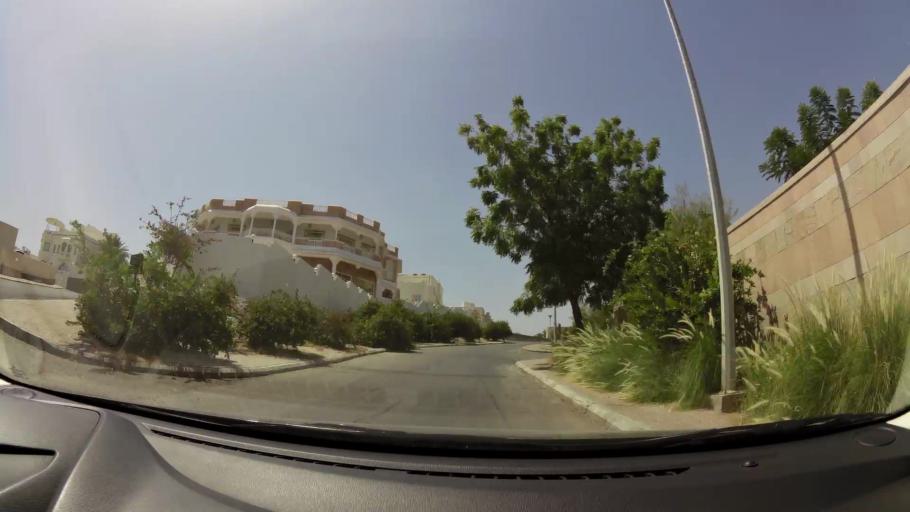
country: OM
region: Muhafazat Masqat
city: Bawshar
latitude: 23.5961
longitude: 58.4544
